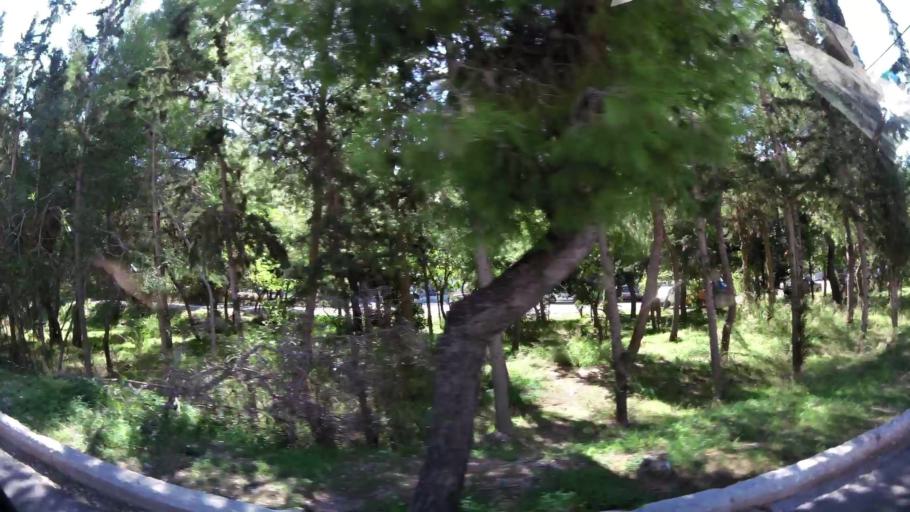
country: GR
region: Attica
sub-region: Nomarchia Anatolikis Attikis
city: Voula
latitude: 37.8534
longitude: 23.7809
